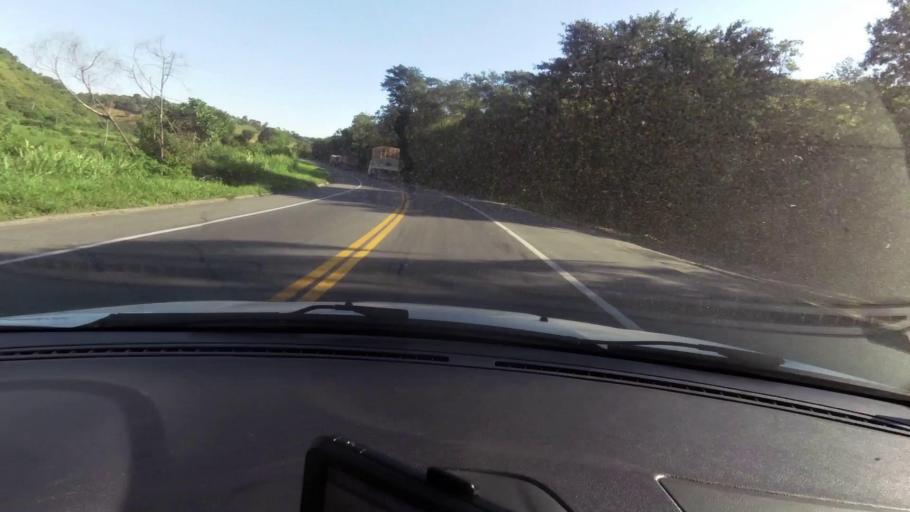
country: BR
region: Espirito Santo
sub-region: Alfredo Chaves
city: Alfredo Chaves
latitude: -20.6549
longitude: -40.6458
